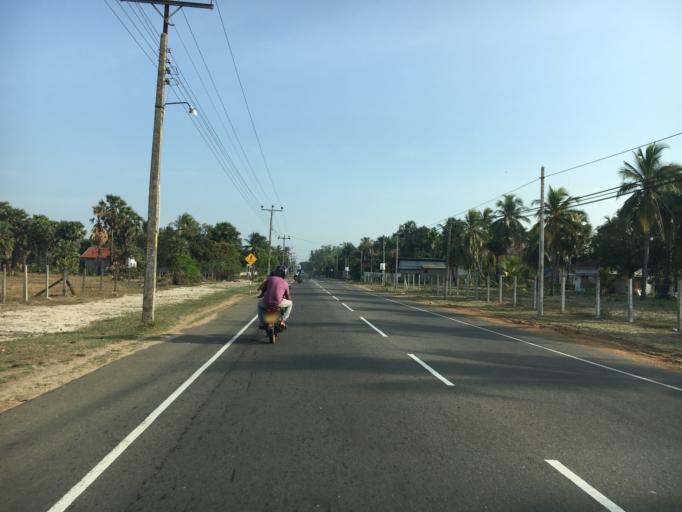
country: LK
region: Eastern Province
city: Eravur Town
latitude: 7.8991
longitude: 81.5358
